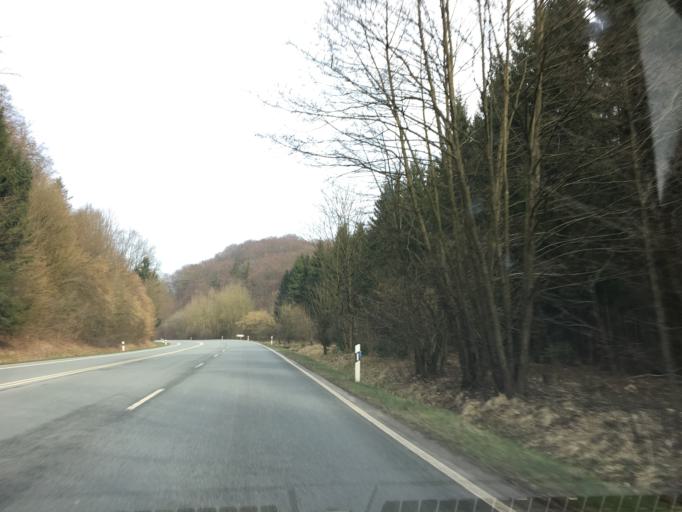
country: DE
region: North Rhine-Westphalia
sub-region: Regierungsbezirk Detmold
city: Willebadessen
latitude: 51.5479
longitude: 9.0125
